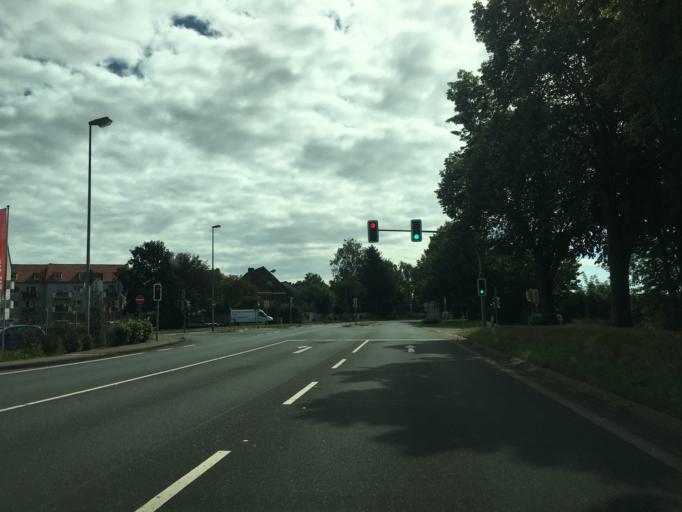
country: DE
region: Lower Saxony
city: Hameln
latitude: 52.1194
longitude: 9.3375
